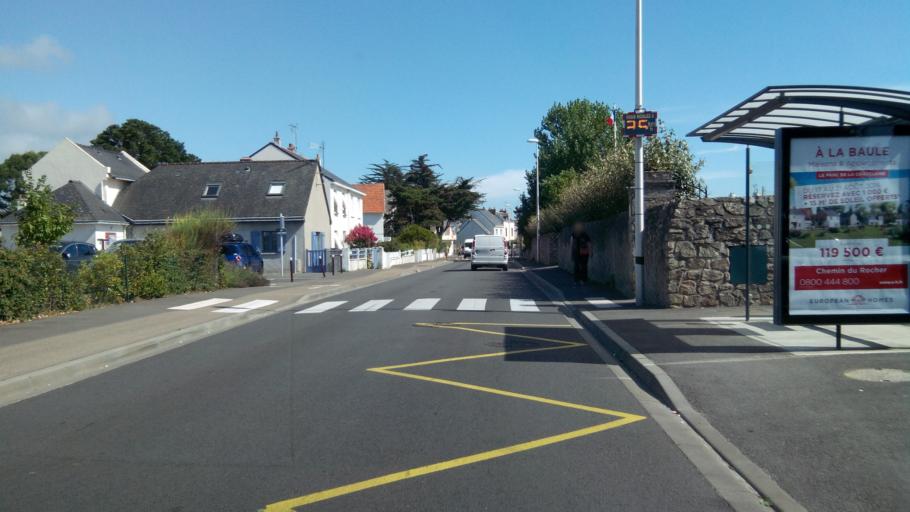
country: FR
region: Pays de la Loire
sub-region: Departement de la Loire-Atlantique
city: Le Croisic
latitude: 47.2895
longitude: -2.5123
